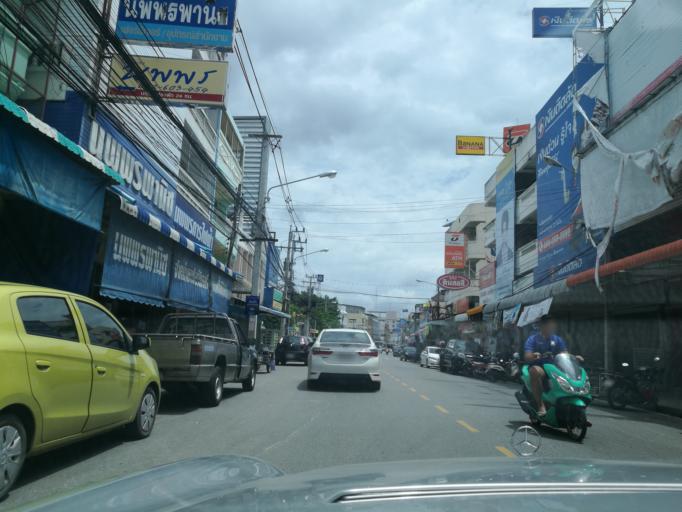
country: TH
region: Prachuap Khiri Khan
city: Prachuap Khiri Khan
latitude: 11.8026
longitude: 99.7979
